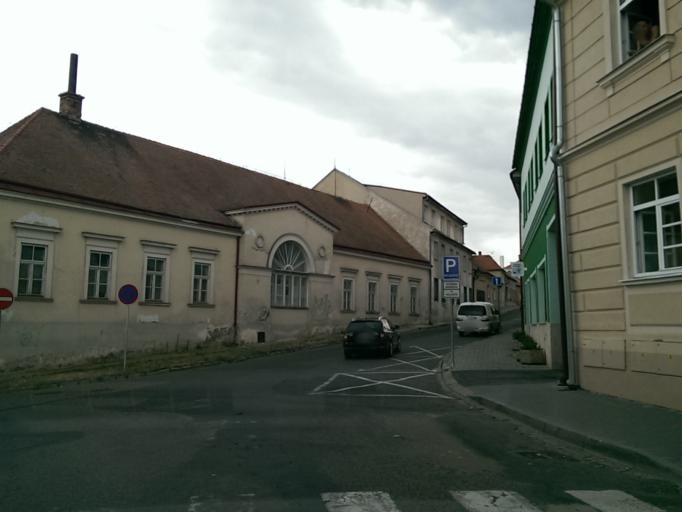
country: CZ
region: South Moravian
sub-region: Okres Breclav
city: Mikulov
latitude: 48.8032
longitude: 16.6396
